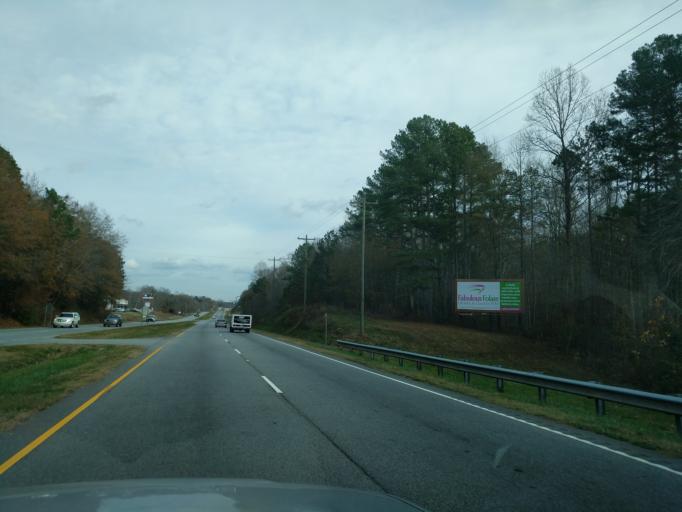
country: US
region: South Carolina
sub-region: Oconee County
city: Utica
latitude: 34.6998
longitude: -82.9295
